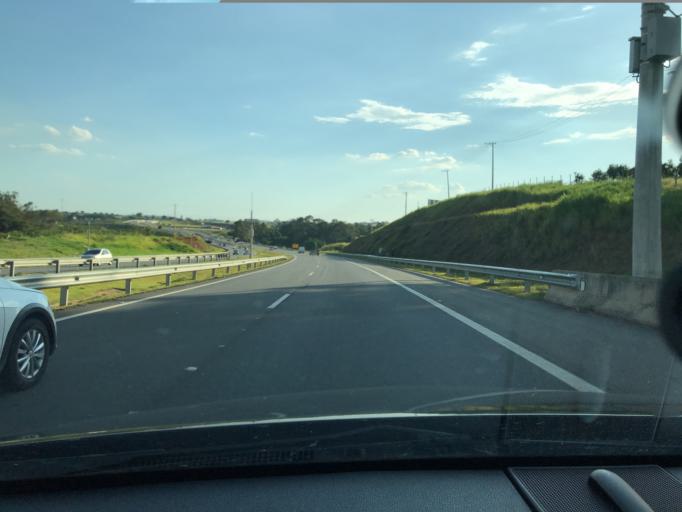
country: BR
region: Sao Paulo
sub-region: Valinhos
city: Valinhos
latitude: -23.0044
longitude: -47.0829
